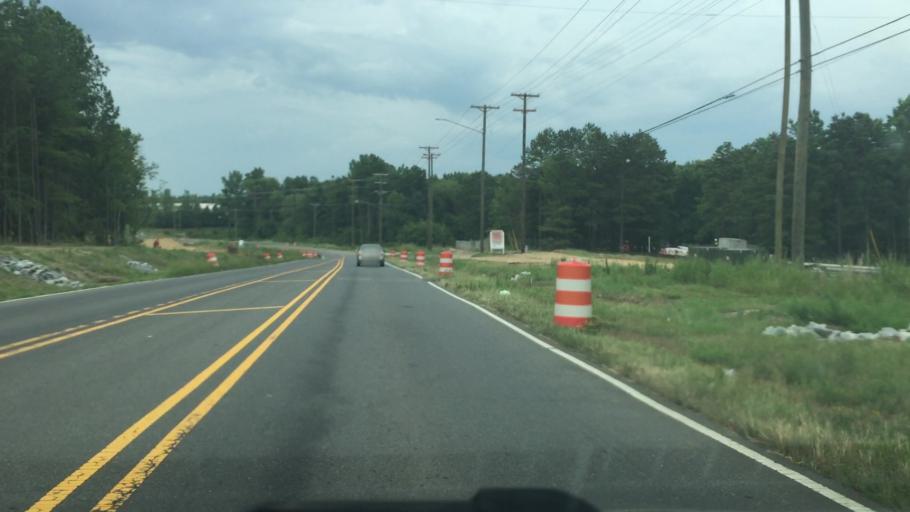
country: US
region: North Carolina
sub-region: Cabarrus County
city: Harrisburg
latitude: 35.3810
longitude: -80.7240
